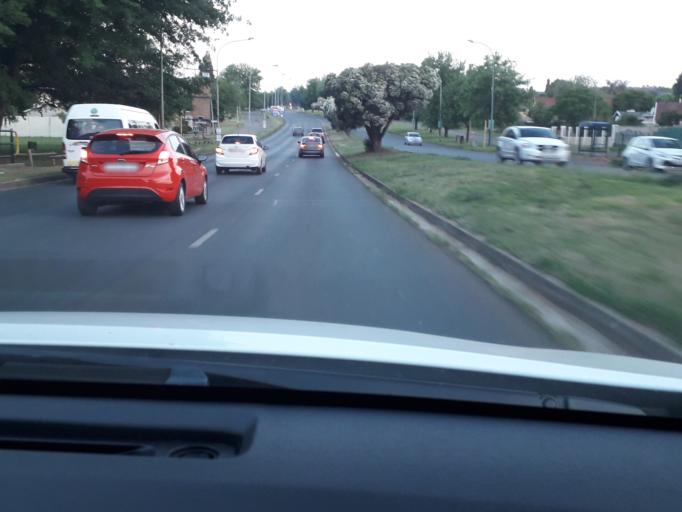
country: ZA
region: Gauteng
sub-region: City of Johannesburg Metropolitan Municipality
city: Johannesburg
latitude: -26.1536
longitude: 27.9902
